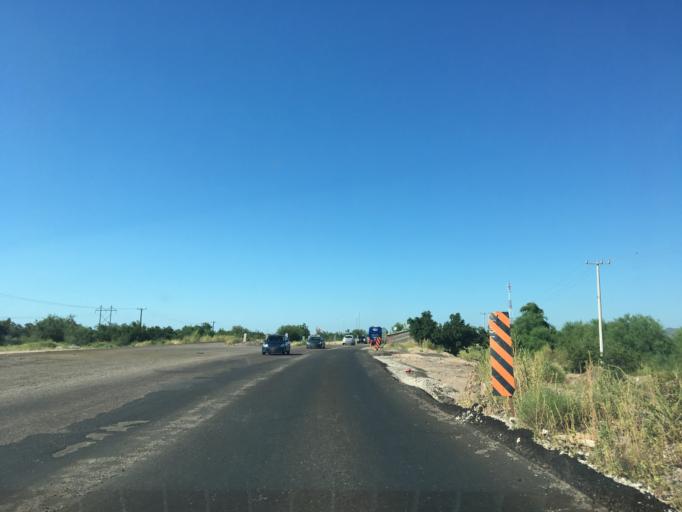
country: MX
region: Sonora
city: Heroica Guaymas
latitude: 28.0357
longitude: -110.9371
